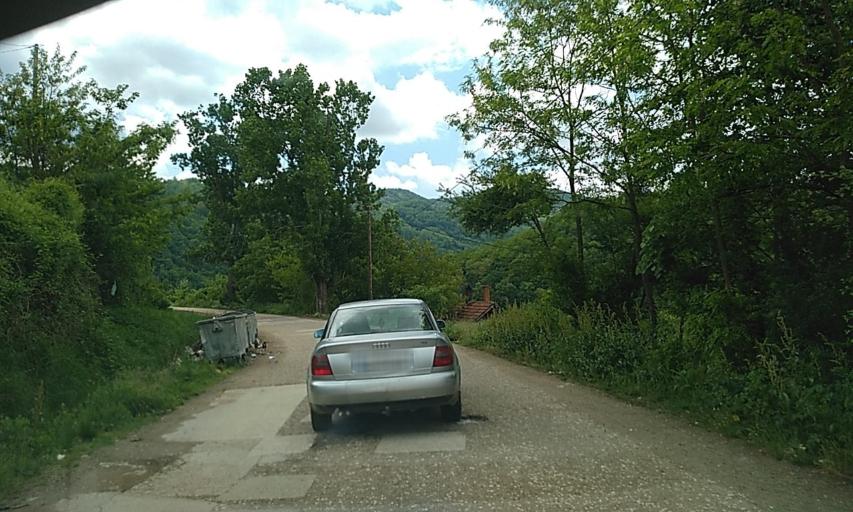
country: RS
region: Central Serbia
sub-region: Pcinjski Okrug
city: Vladicin Han
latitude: 42.7210
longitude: 22.0661
